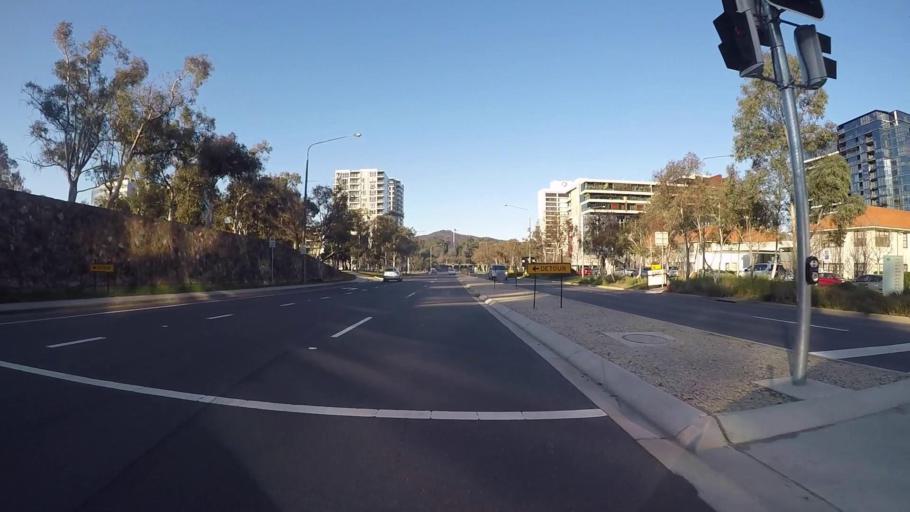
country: AU
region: Australian Capital Territory
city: Canberra
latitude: -35.2843
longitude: 149.1229
